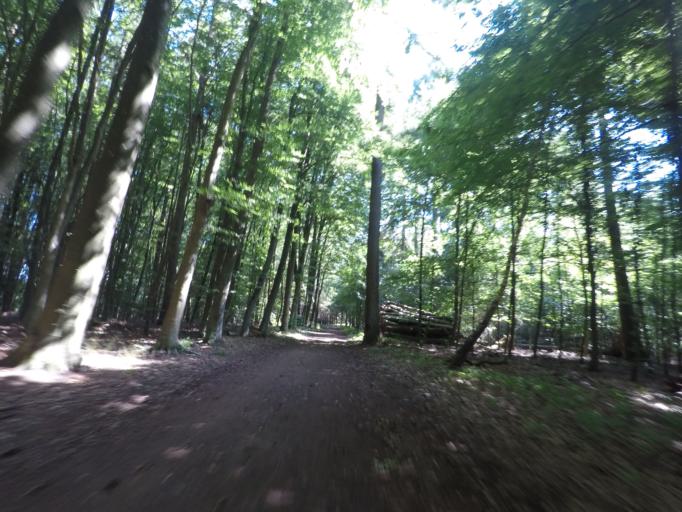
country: LU
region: Luxembourg
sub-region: Canton de Luxembourg
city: Strassen
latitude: 49.6278
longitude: 6.0933
